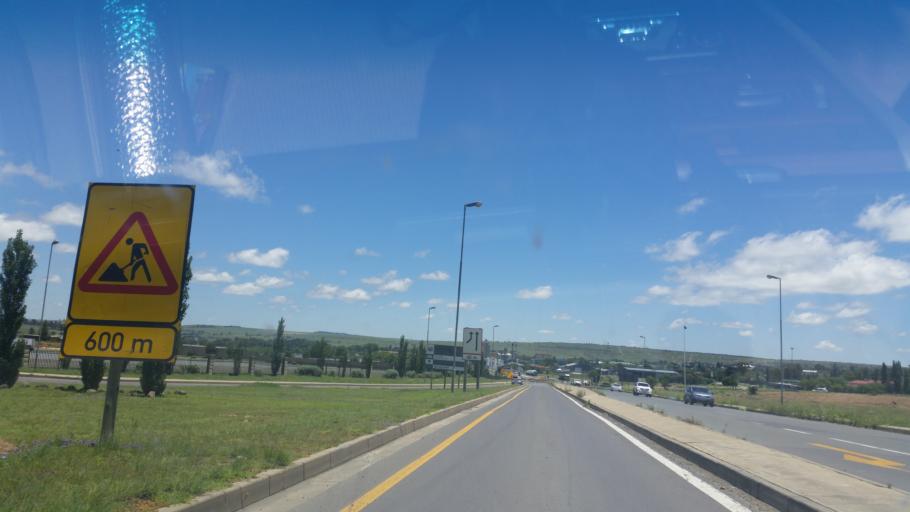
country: ZA
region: Orange Free State
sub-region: Thabo Mofutsanyana District Municipality
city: Harrismith
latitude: -28.2878
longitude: 29.1337
